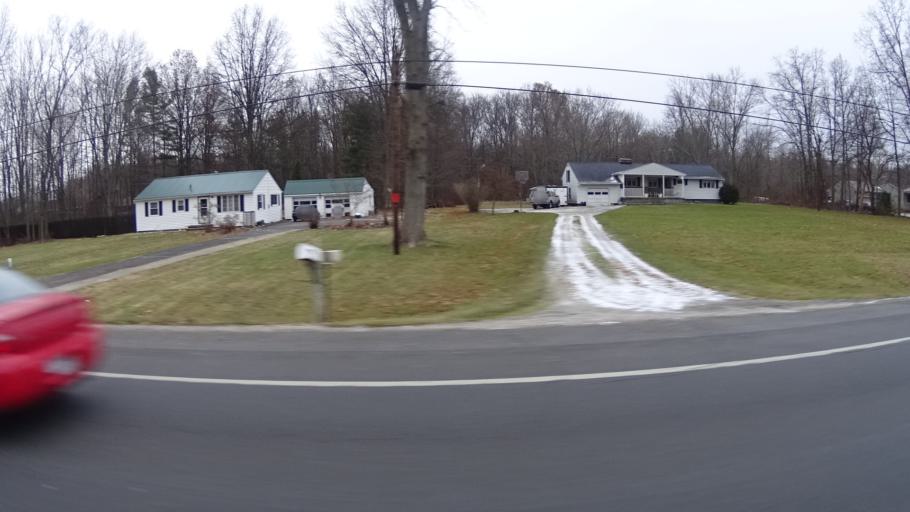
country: US
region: Ohio
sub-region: Lorain County
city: Eaton Estates
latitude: 41.3148
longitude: -82.0440
